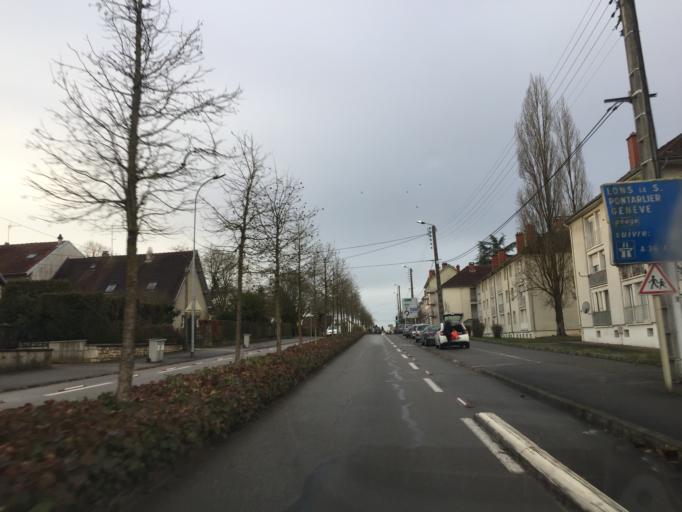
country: FR
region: Franche-Comte
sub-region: Departement du Jura
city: Dole
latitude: 47.0753
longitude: 5.4985
